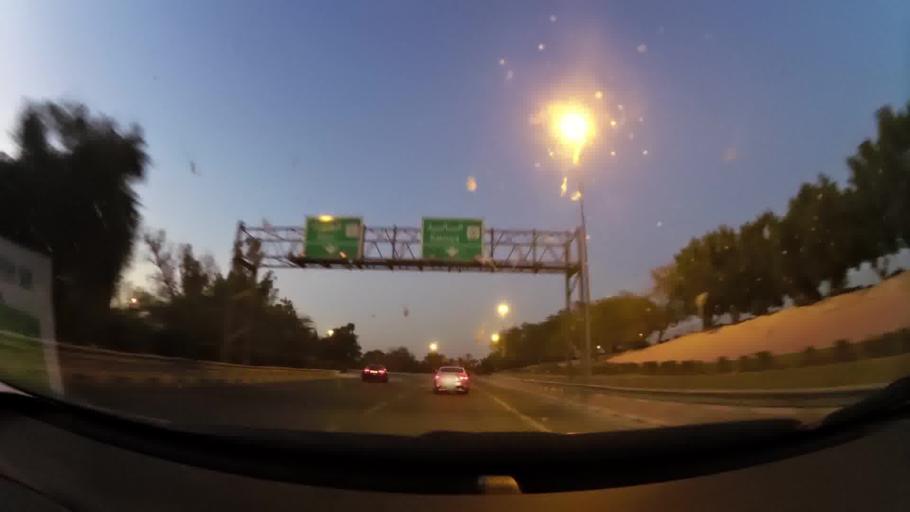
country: KW
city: Bayan
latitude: 29.3032
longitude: 48.0246
